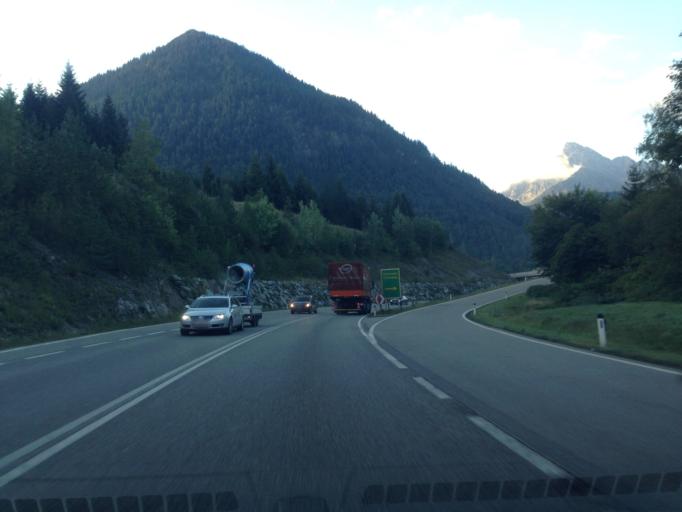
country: AT
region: Tyrol
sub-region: Politischer Bezirk Reutte
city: Breitenwang
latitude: 47.4918
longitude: 10.7480
